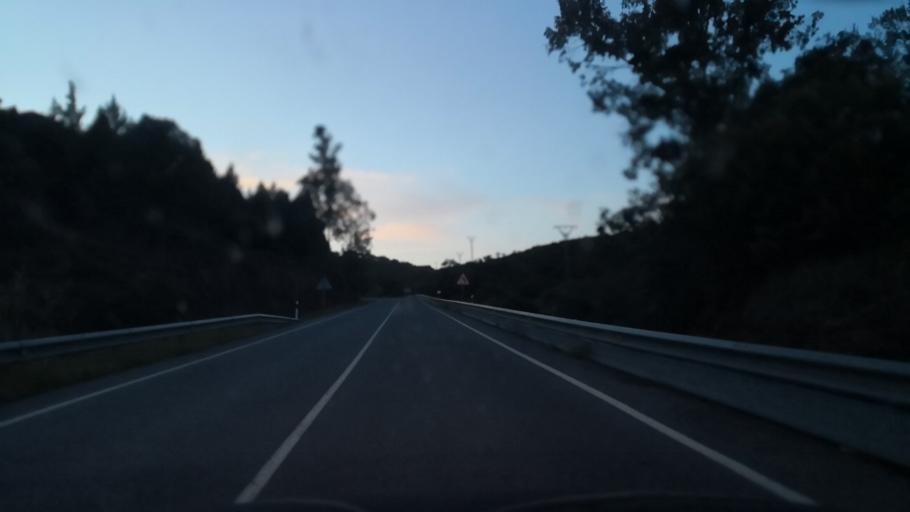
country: ES
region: Extremadura
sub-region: Provincia de Caceres
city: Alcantara
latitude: 39.7311
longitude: -6.8952
